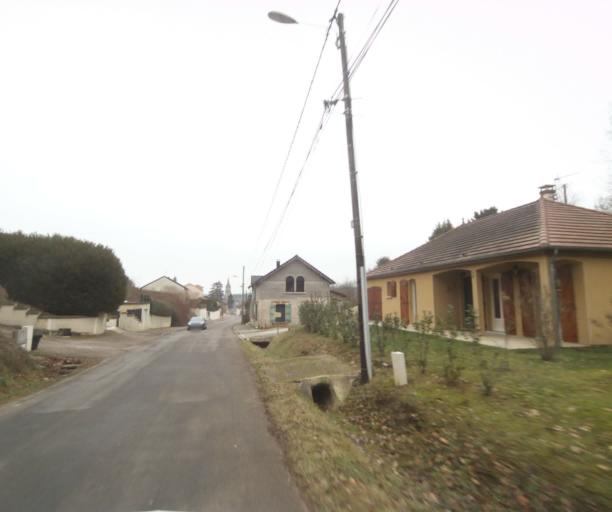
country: FR
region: Champagne-Ardenne
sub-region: Departement de la Haute-Marne
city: Bienville
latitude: 48.5808
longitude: 5.0343
